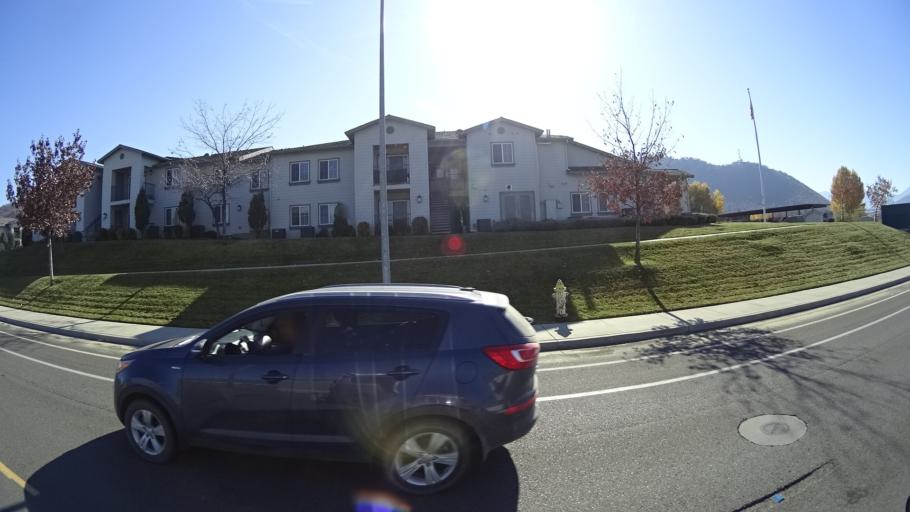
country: US
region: California
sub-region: Siskiyou County
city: Yreka
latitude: 41.7340
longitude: -122.6276
